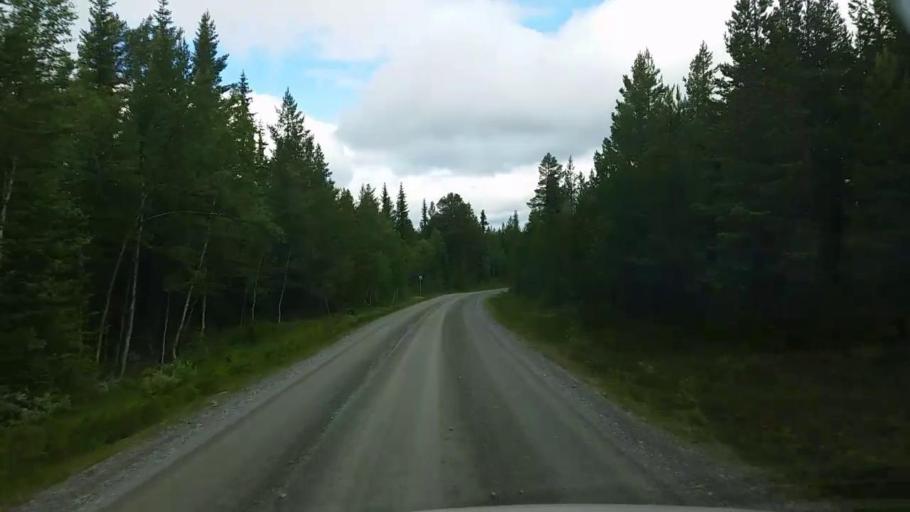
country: NO
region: Hedmark
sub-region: Engerdal
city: Engerdal
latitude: 62.4030
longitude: 12.6640
